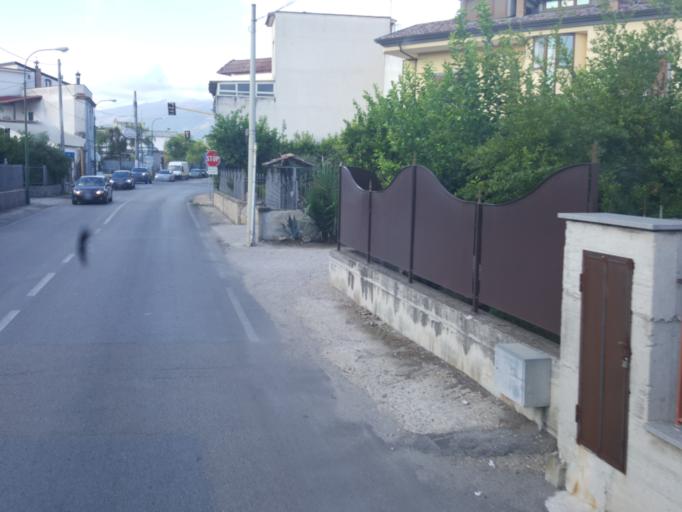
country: IT
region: Campania
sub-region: Provincia di Napoli
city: Piazzolla
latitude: 40.8858
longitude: 14.5122
